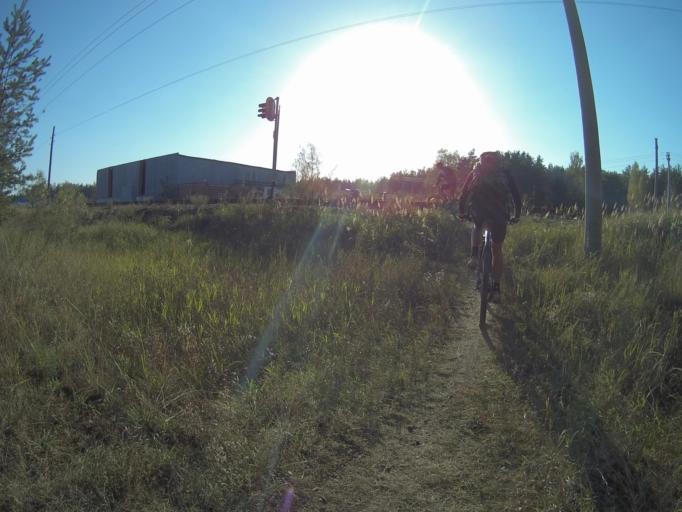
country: RU
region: Vladimir
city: Raduzhnyy
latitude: 56.0300
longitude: 40.3844
